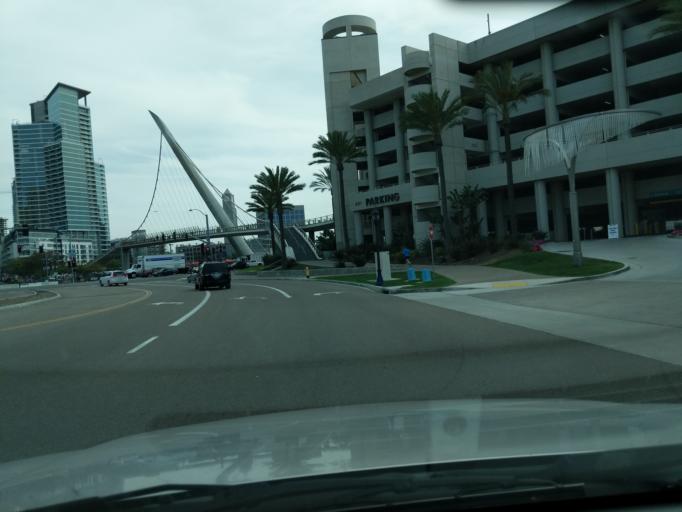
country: US
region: California
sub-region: San Diego County
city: San Diego
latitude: 32.7045
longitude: -117.1584
